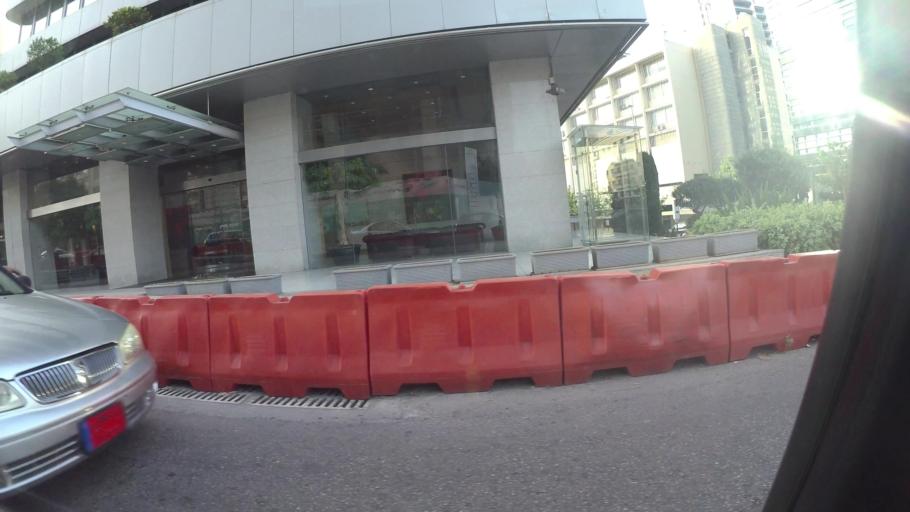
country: LB
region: Beyrouth
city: Beirut
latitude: 33.8976
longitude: 35.4956
